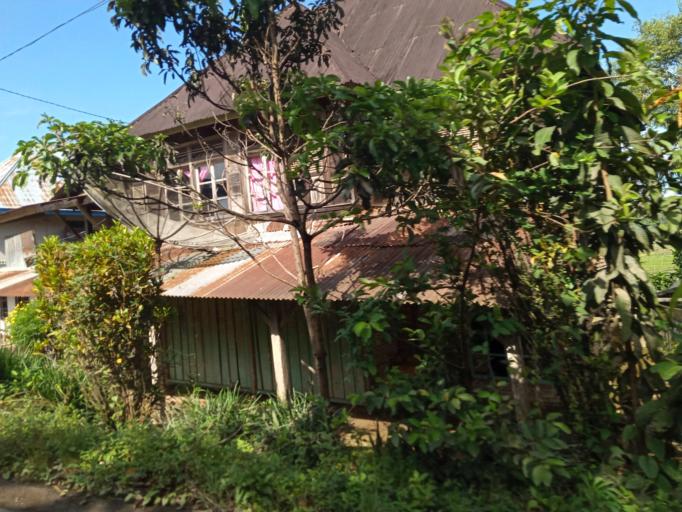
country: ID
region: Jambi
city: Sungai Penuh
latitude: -2.1686
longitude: 101.5971
